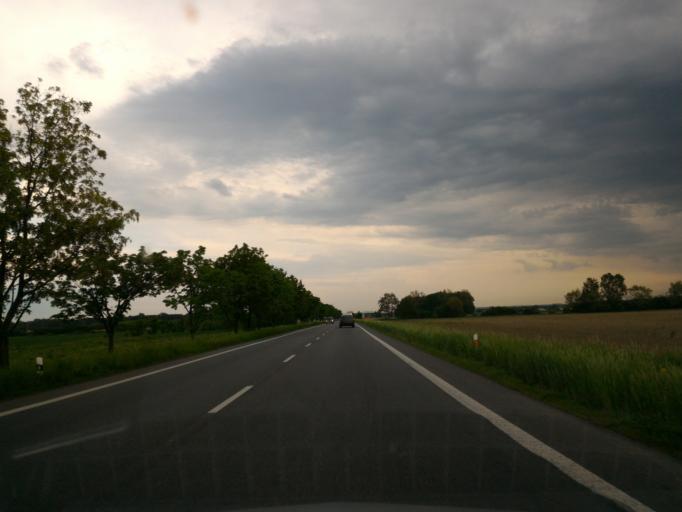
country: CZ
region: Central Bohemia
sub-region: Okres Nymburk
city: Podebrady
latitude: 50.1471
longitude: 15.0903
